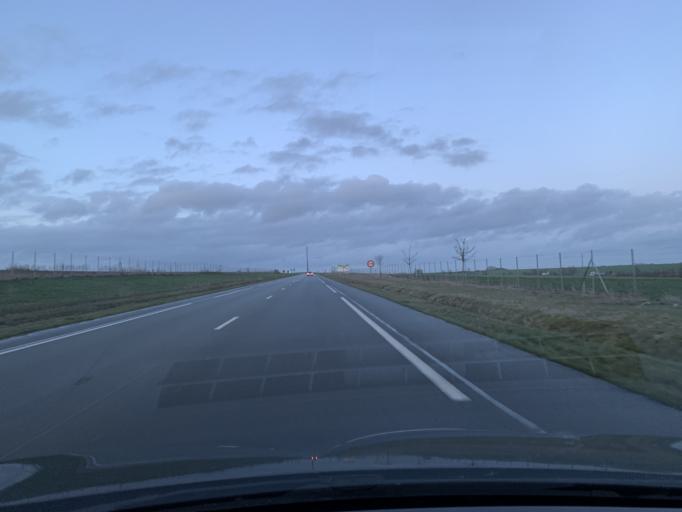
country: FR
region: Nord-Pas-de-Calais
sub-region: Departement du Nord
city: Escaudoeuvres
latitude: 50.1567
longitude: 3.2962
